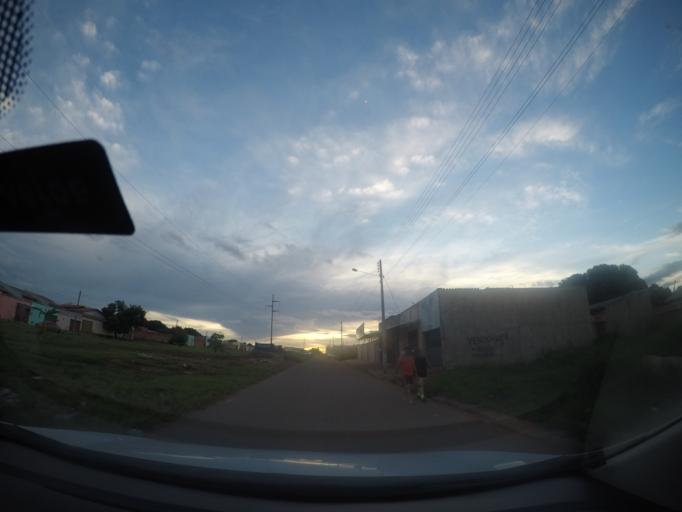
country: BR
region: Goias
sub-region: Goianira
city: Goianira
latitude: -16.5724
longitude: -49.3867
